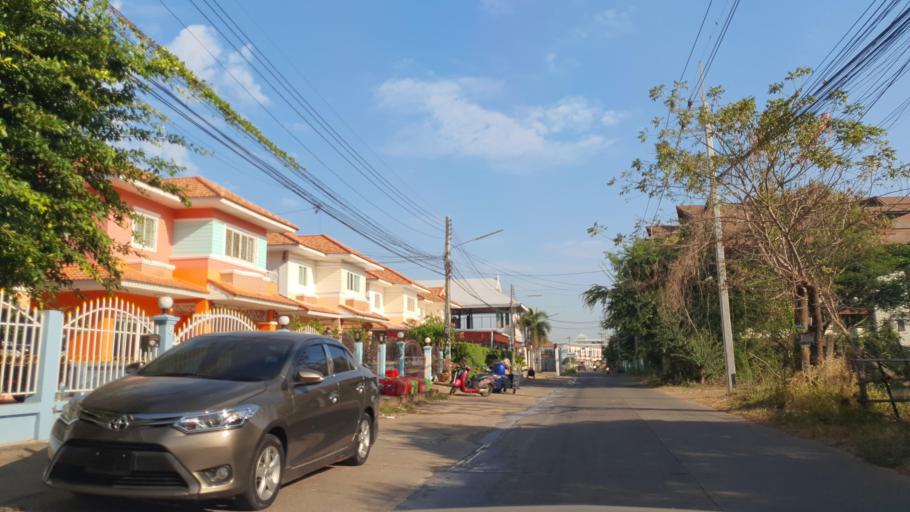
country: TH
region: Khon Kaen
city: Khon Kaen
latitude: 16.4163
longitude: 102.8037
